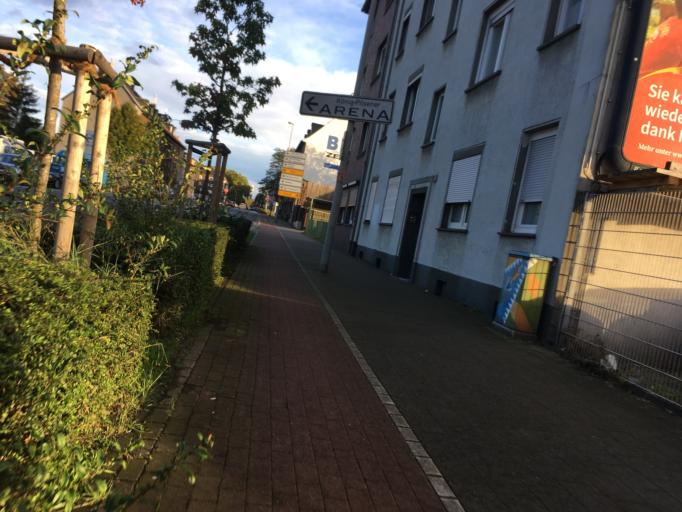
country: DE
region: North Rhine-Westphalia
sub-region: Regierungsbezirk Dusseldorf
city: Oberhausen
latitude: 51.4810
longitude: 6.8448
